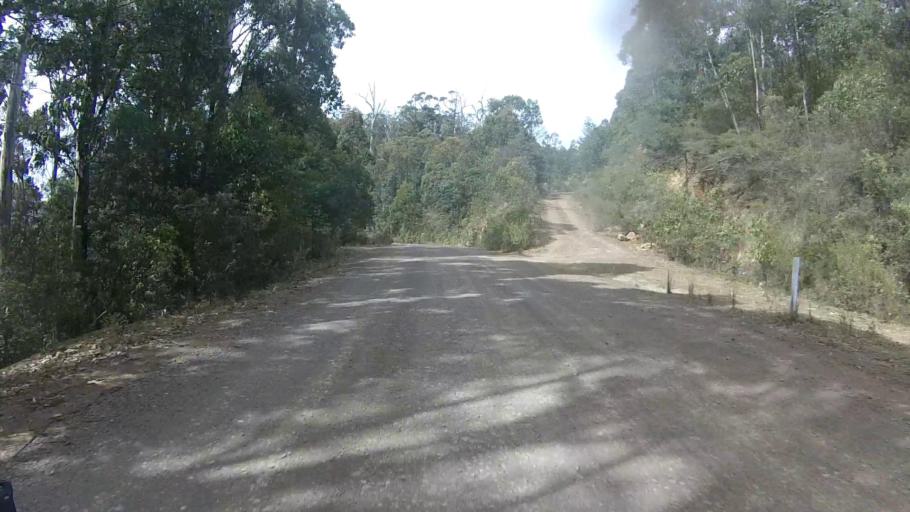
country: AU
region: Tasmania
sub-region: Sorell
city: Sorell
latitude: -42.7600
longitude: 147.8290
